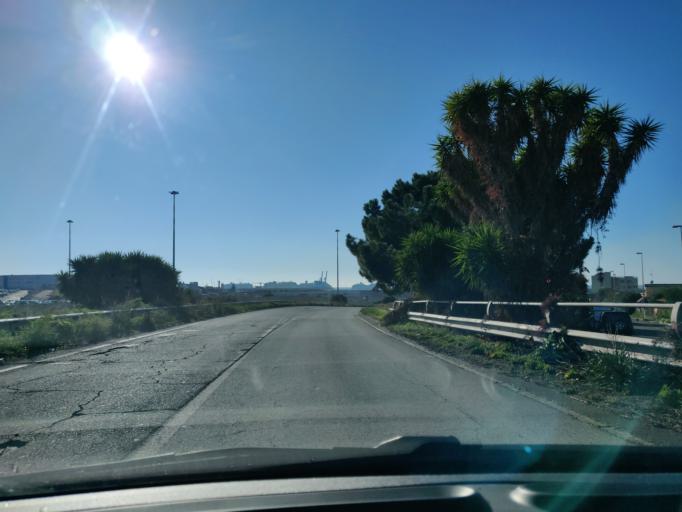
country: IT
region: Latium
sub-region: Citta metropolitana di Roma Capitale
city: Aurelia
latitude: 42.1281
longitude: 11.7730
